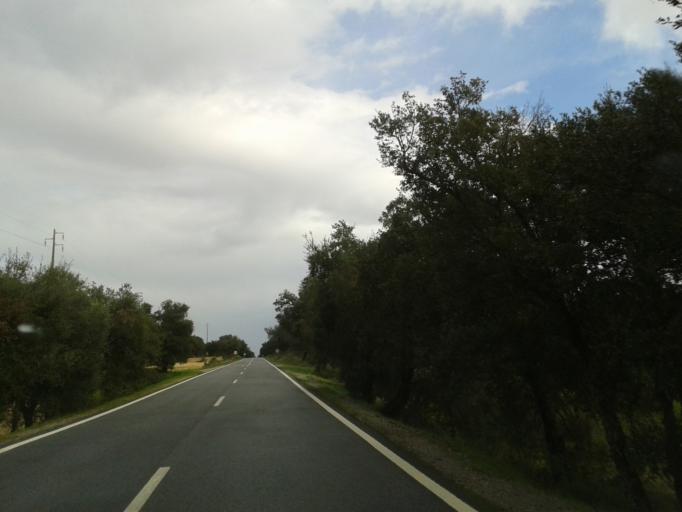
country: PT
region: Santarem
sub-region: Benavente
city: Poceirao
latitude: 38.8152
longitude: -8.7842
